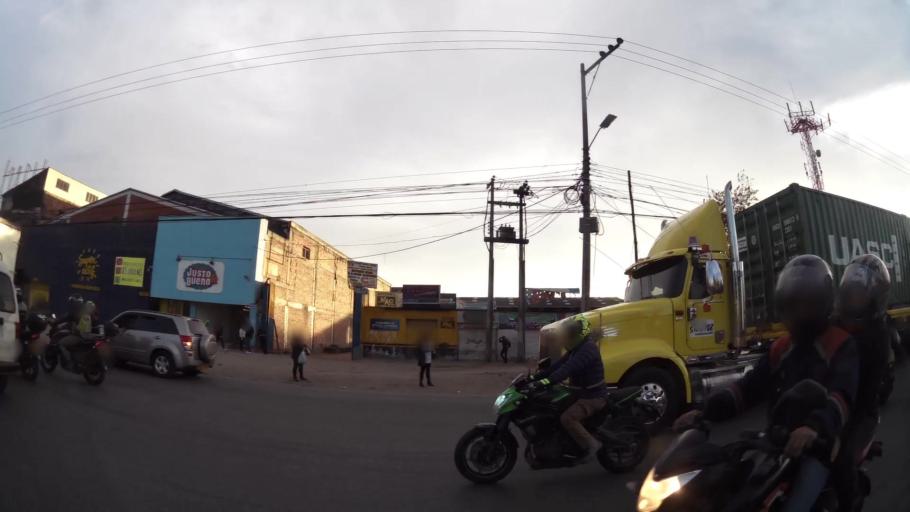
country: CO
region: Cundinamarca
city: Funza
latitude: 4.6904
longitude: -74.1642
